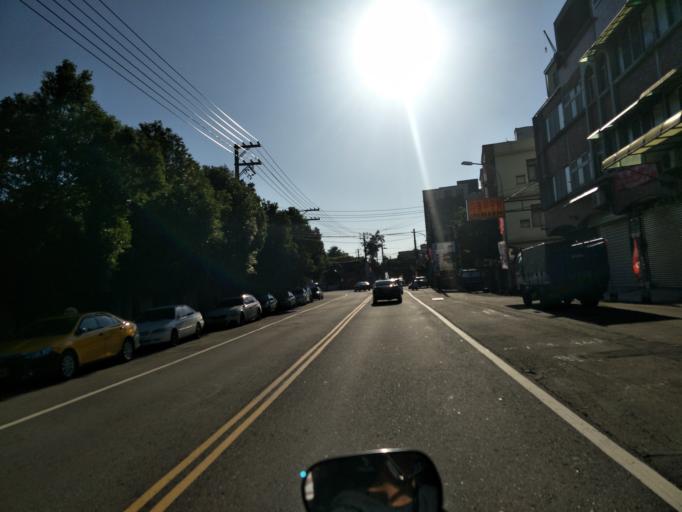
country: TW
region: Taiwan
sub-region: Hsinchu
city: Zhubei
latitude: 24.8712
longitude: 121.0375
